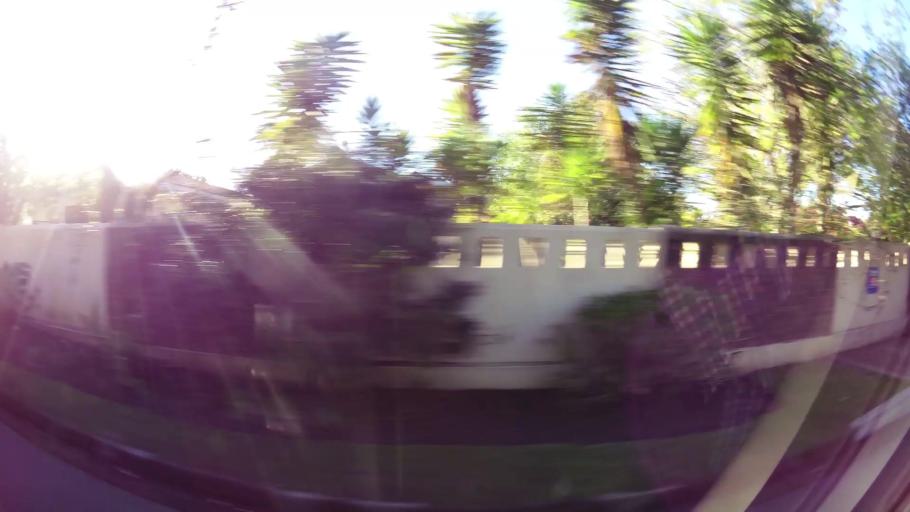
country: ZA
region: Western Cape
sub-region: Eden District Municipality
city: George
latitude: -33.9442
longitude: 22.4566
